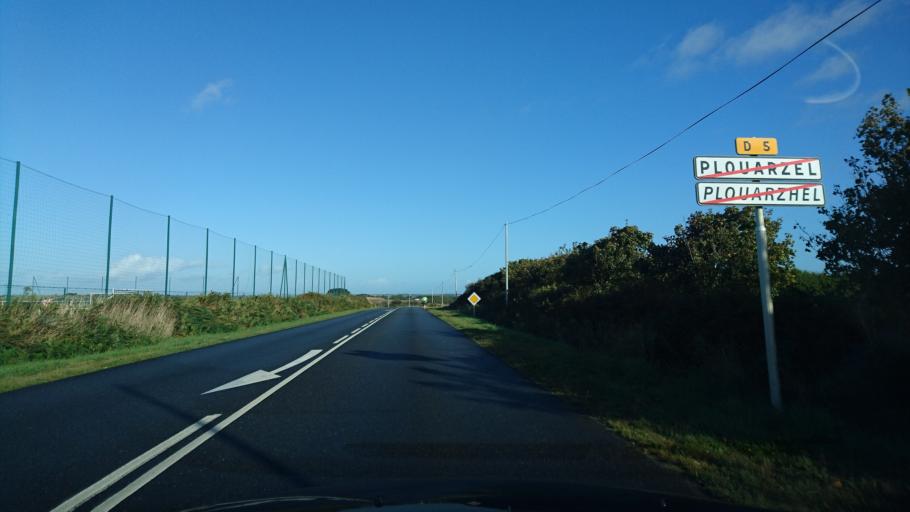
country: FR
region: Brittany
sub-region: Departement du Finistere
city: Plouarzel
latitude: 48.4351
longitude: -4.7154
